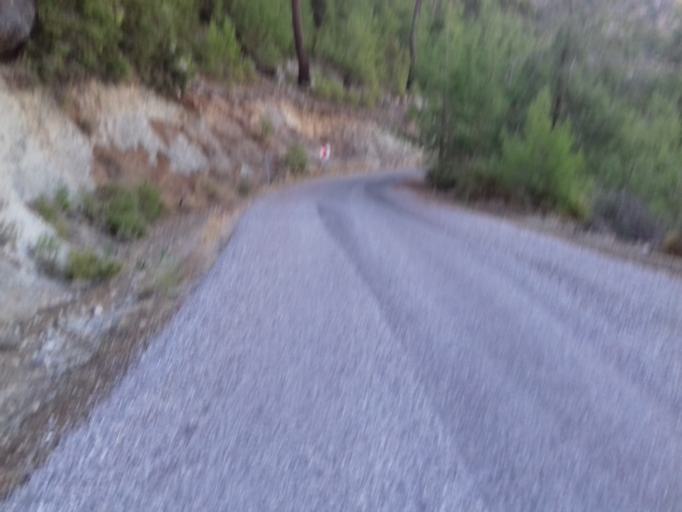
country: TR
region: Mugla
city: Yaniklar
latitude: 36.7829
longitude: 29.0186
